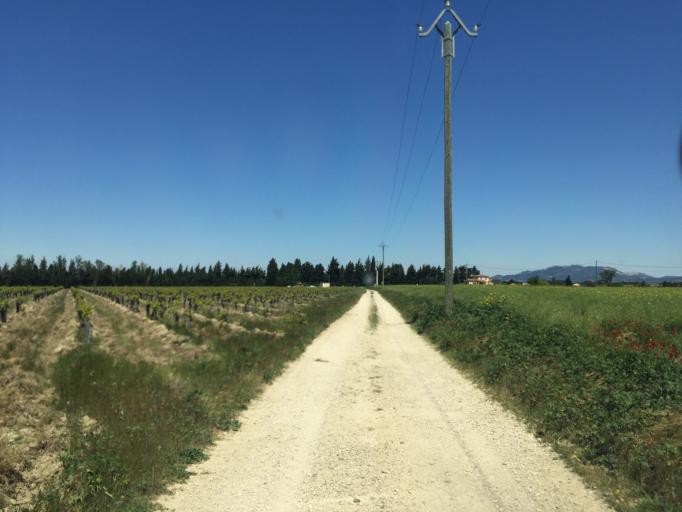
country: FR
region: Provence-Alpes-Cote d'Azur
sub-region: Departement du Vaucluse
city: Courthezon
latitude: 44.0702
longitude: 4.9050
